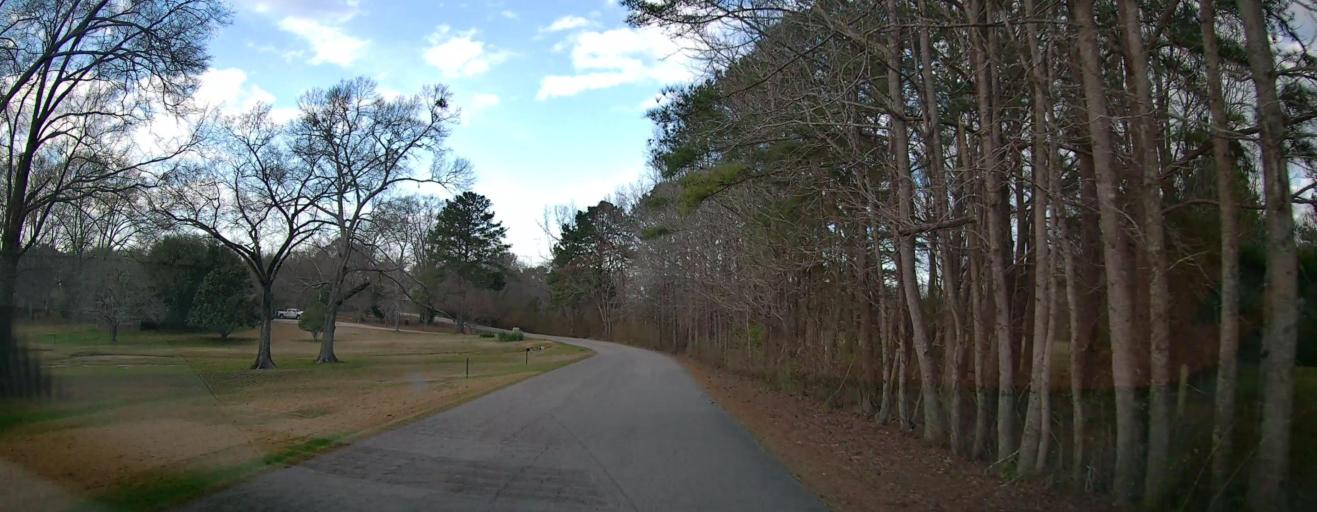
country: US
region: Georgia
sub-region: Harris County
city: Hamilton
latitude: 32.6803
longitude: -84.7439
